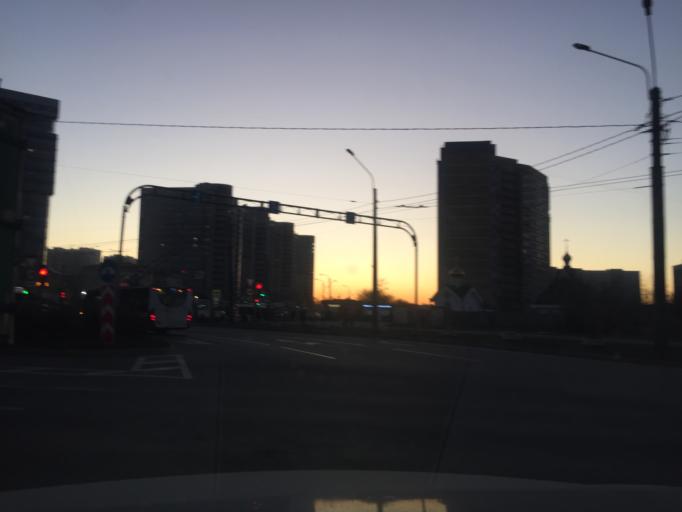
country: RU
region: St.-Petersburg
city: Obukhovo
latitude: 59.8662
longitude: 30.4147
